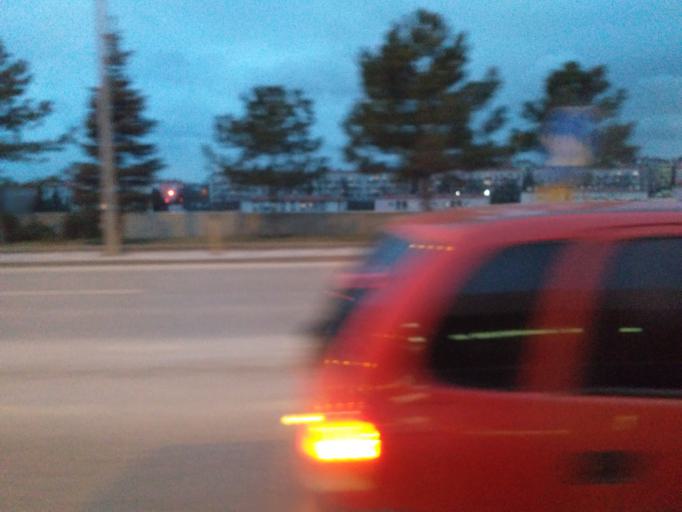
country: TR
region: Ankara
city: Ankara
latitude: 39.9620
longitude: 32.8218
